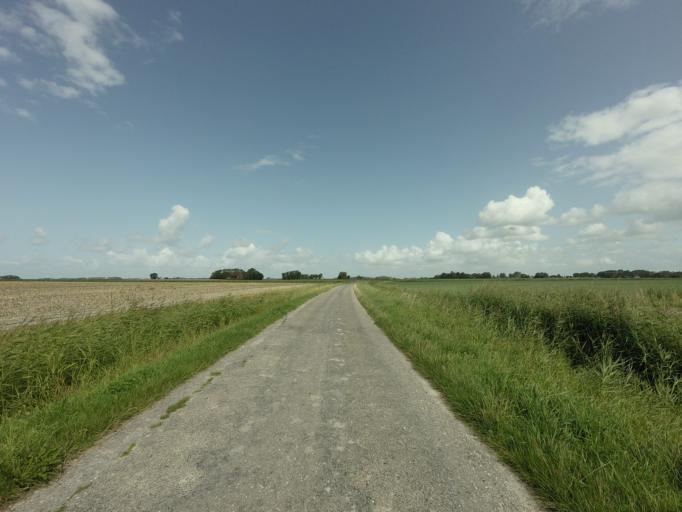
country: NL
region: Friesland
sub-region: Gemeente Harlingen
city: Harlingen
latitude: 53.1182
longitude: 5.4381
